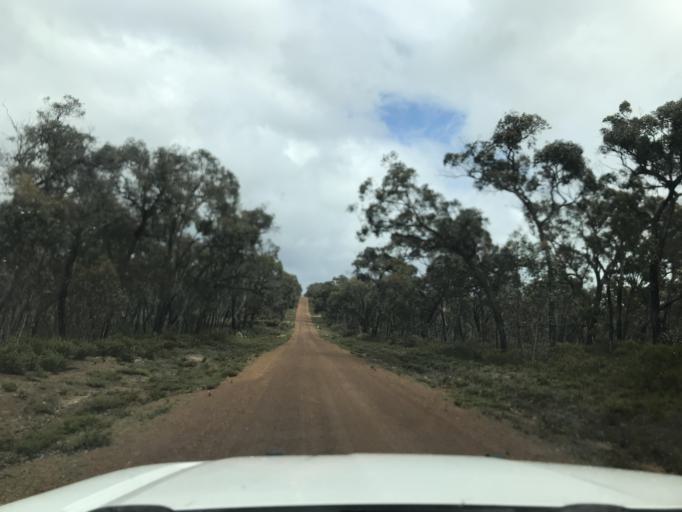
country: AU
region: South Australia
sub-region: Wattle Range
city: Penola
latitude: -37.2950
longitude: 141.3158
